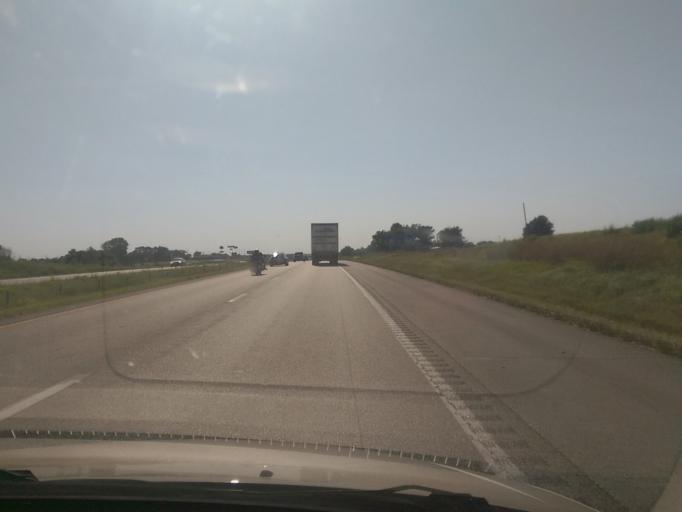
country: US
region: Missouri
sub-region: Saline County
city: Sweet Springs
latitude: 38.9770
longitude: -93.4062
